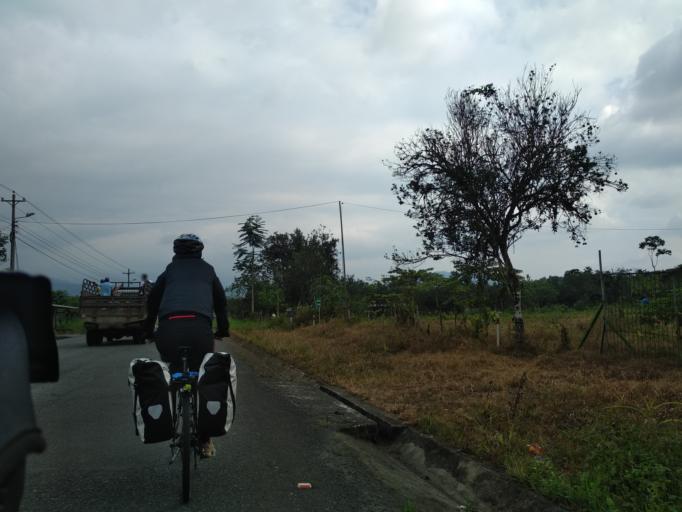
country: EC
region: Cotopaxi
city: La Mana
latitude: -0.8929
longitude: -79.1616
